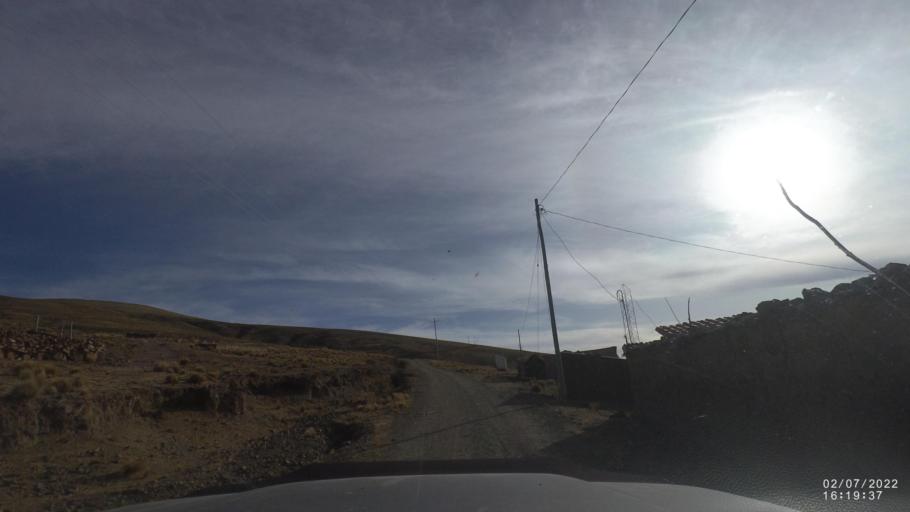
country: BO
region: Cochabamba
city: Irpa Irpa
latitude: -17.9302
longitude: -66.4439
